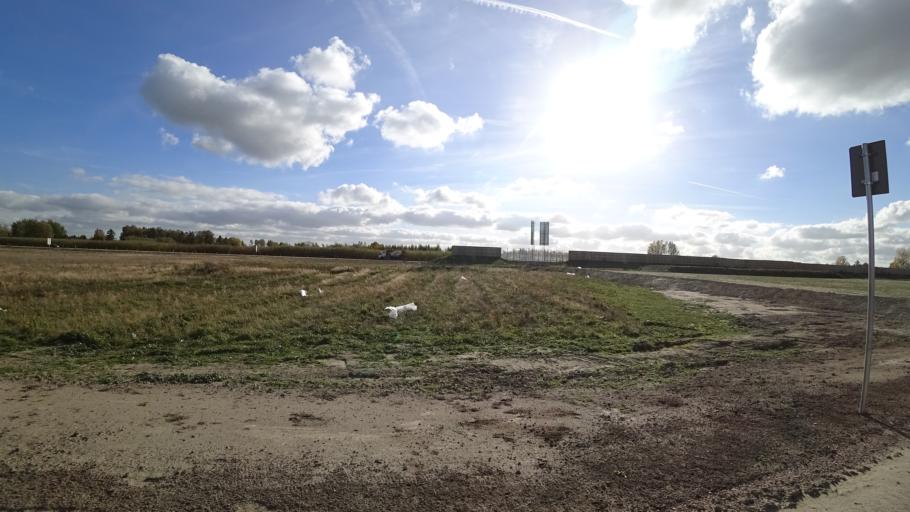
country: SE
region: Skane
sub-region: Staffanstorps Kommun
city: Staffanstorp
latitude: 55.6301
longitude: 13.2093
